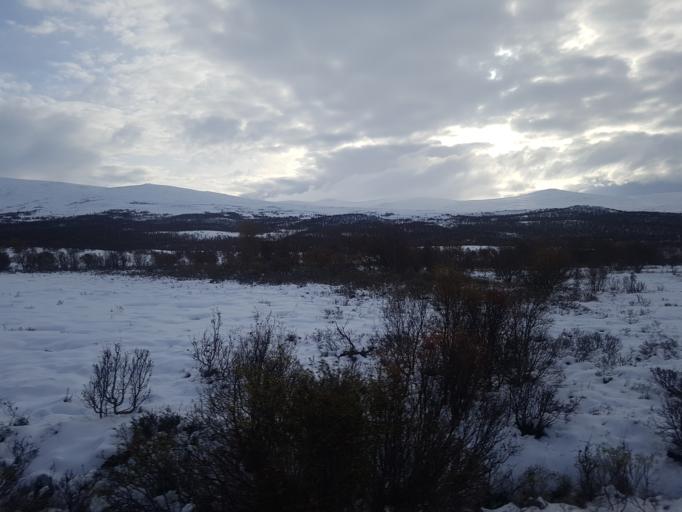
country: NO
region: Oppland
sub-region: Dovre
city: Dovre
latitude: 62.1158
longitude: 9.2827
